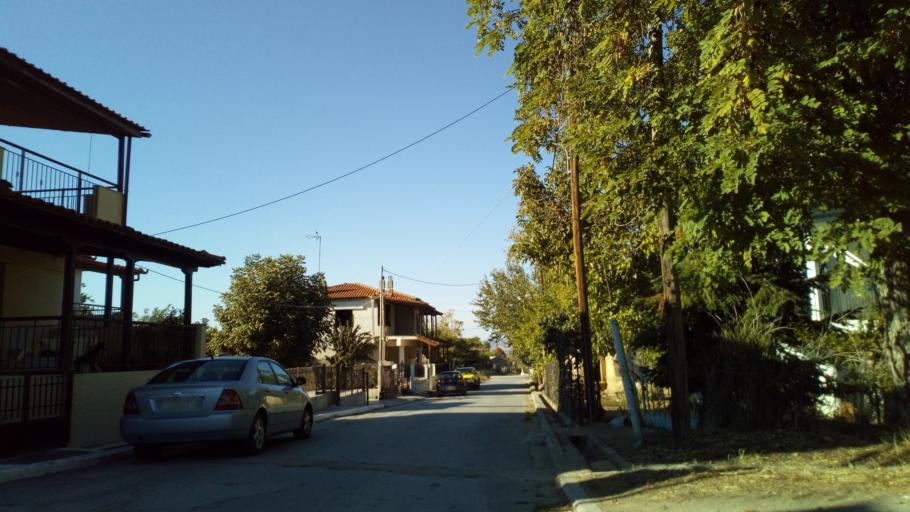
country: GR
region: Central Macedonia
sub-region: Nomos Thessalonikis
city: Gerakarou
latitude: 40.6362
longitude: 23.2477
